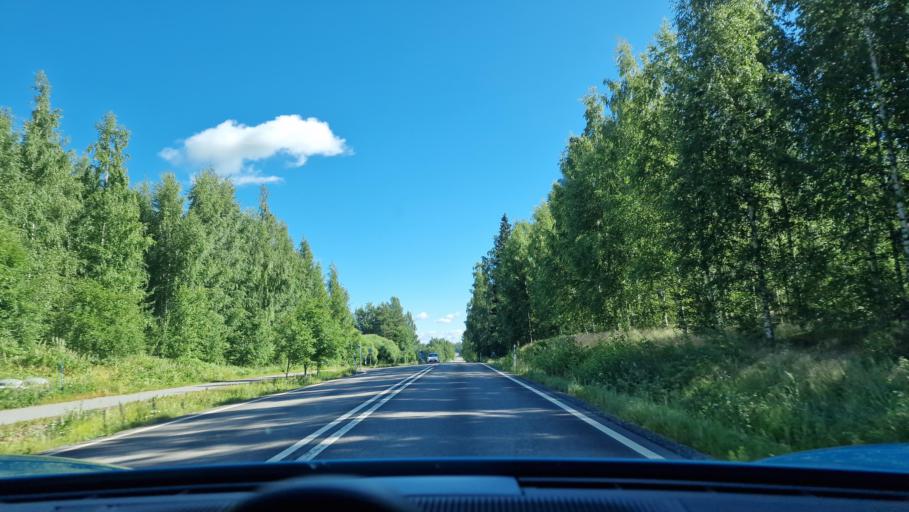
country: FI
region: Pirkanmaa
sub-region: Tampere
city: Kangasala
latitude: 61.4724
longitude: 24.1338
